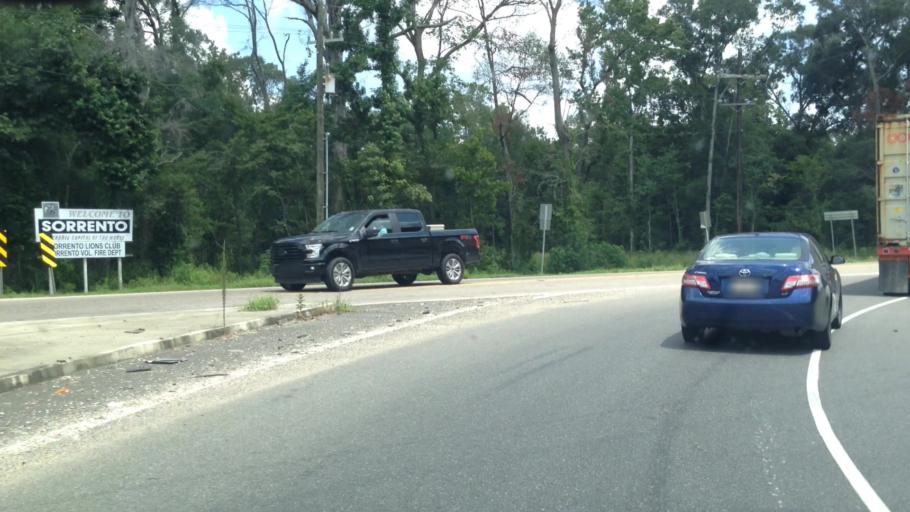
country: US
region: Louisiana
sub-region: Ascension Parish
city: Sorrento
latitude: 30.1666
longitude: -90.8810
